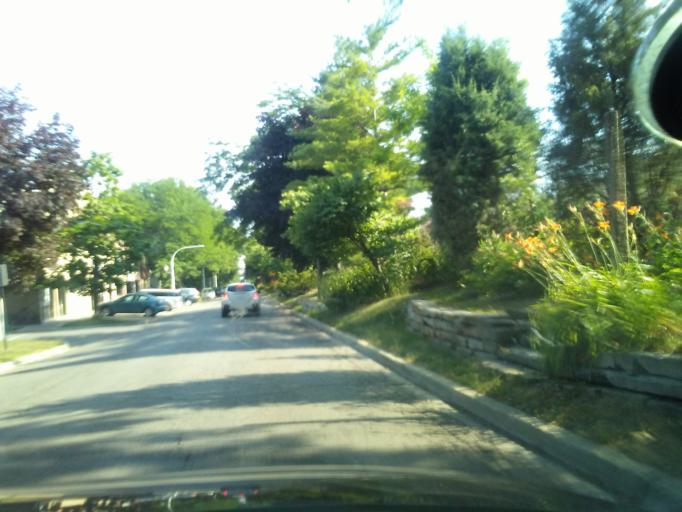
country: US
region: Illinois
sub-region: Cook County
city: Lincolnwood
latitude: 41.9754
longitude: -87.6744
